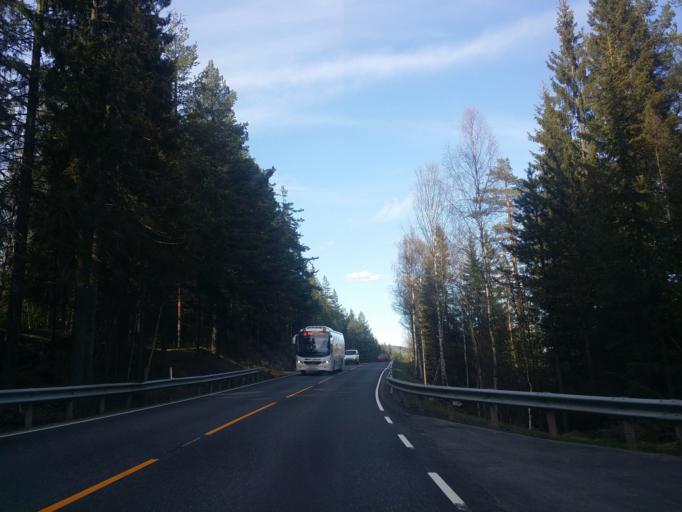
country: NO
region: Buskerud
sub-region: Kongsberg
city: Kongsberg
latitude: 59.6167
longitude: 9.4674
